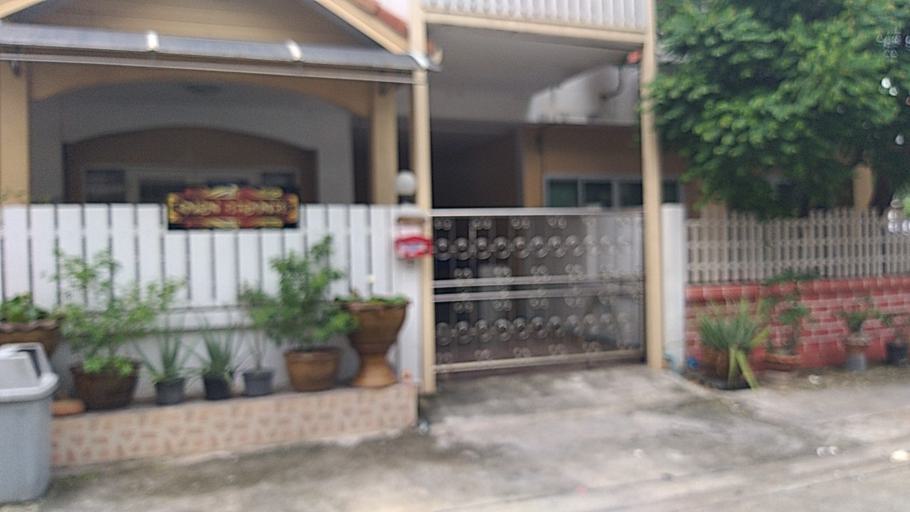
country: TH
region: Bangkok
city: Suan Luang
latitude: 13.7102
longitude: 100.6632
